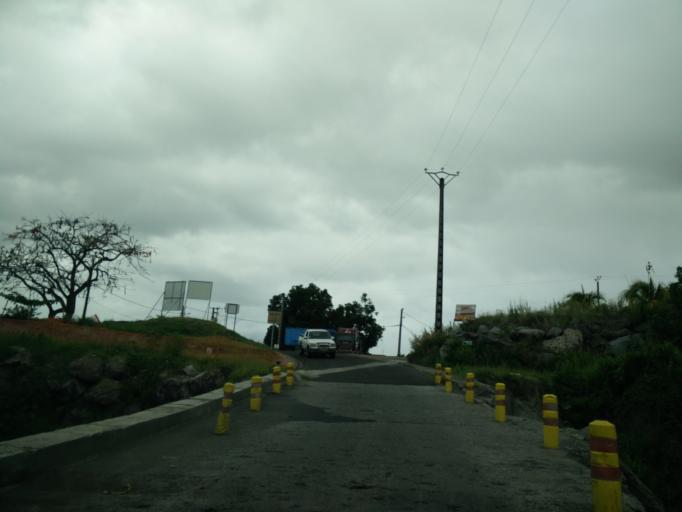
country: MQ
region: Martinique
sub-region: Martinique
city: Saint-Pierre
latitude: 14.8031
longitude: -61.2254
